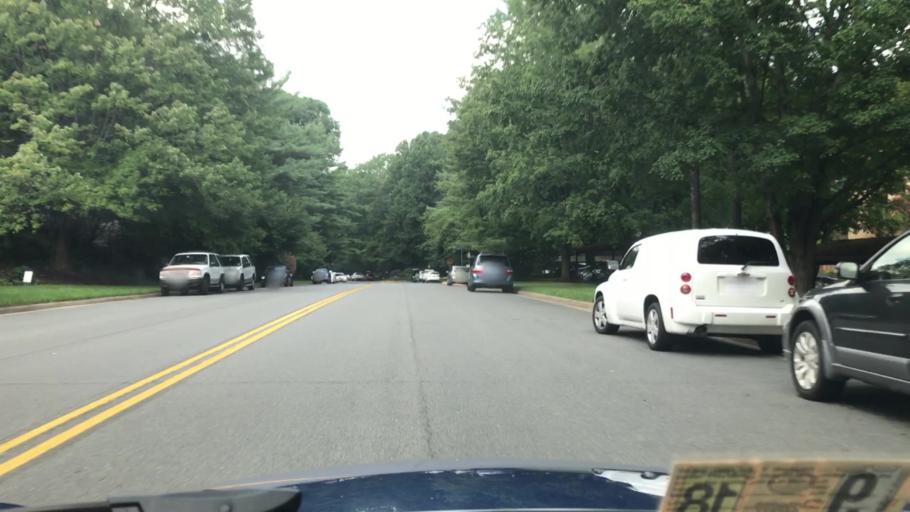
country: US
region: Virginia
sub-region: Fairfax County
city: Reston
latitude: 38.9350
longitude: -77.3340
